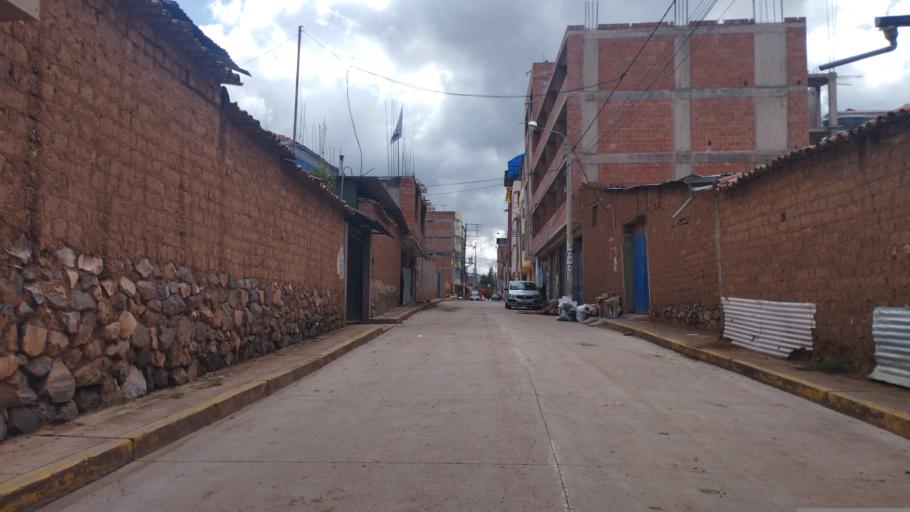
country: PE
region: Cusco
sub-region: Provincia de Cusco
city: Cusco
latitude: -13.5246
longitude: -71.9415
